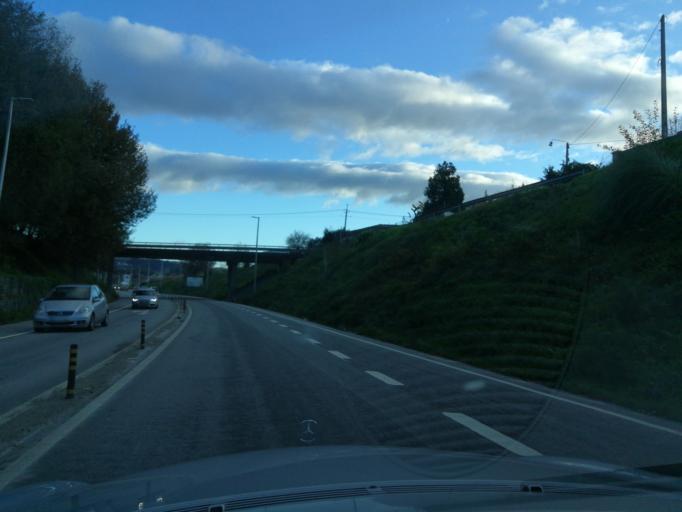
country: PT
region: Braga
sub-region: Barcelos
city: Vila Frescainha
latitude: 41.5300
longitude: -8.6392
